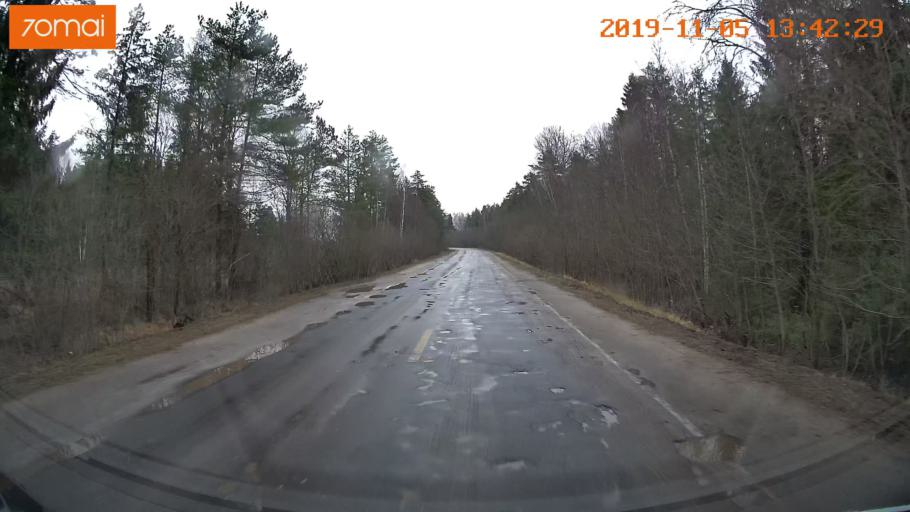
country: RU
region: Ivanovo
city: Shuya
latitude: 56.9669
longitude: 41.3945
